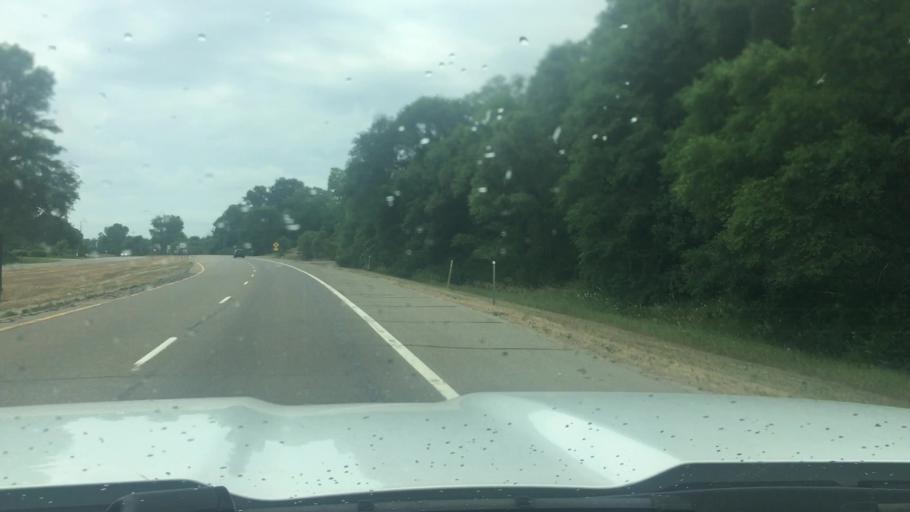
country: US
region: Michigan
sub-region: Kent County
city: Forest Hills
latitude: 42.9632
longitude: -85.5493
